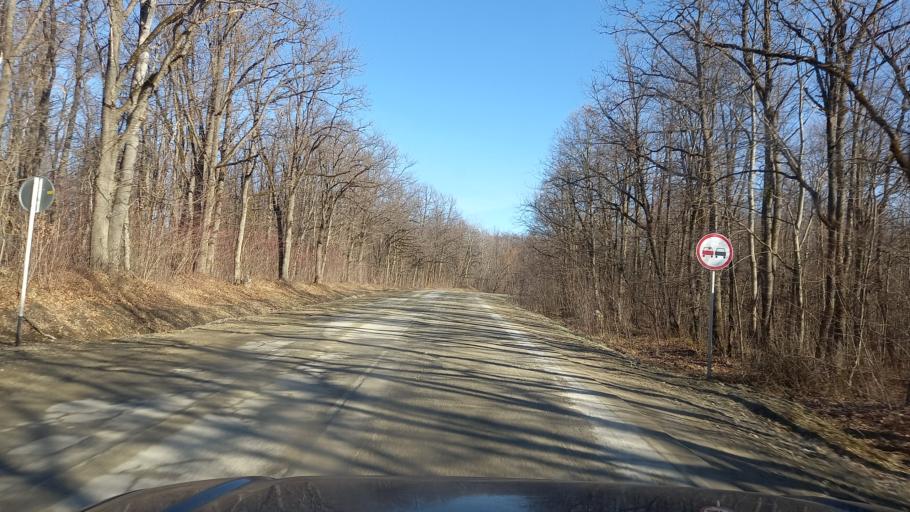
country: RU
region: Adygeya
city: Kamennomostskiy
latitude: 44.2829
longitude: 40.2619
